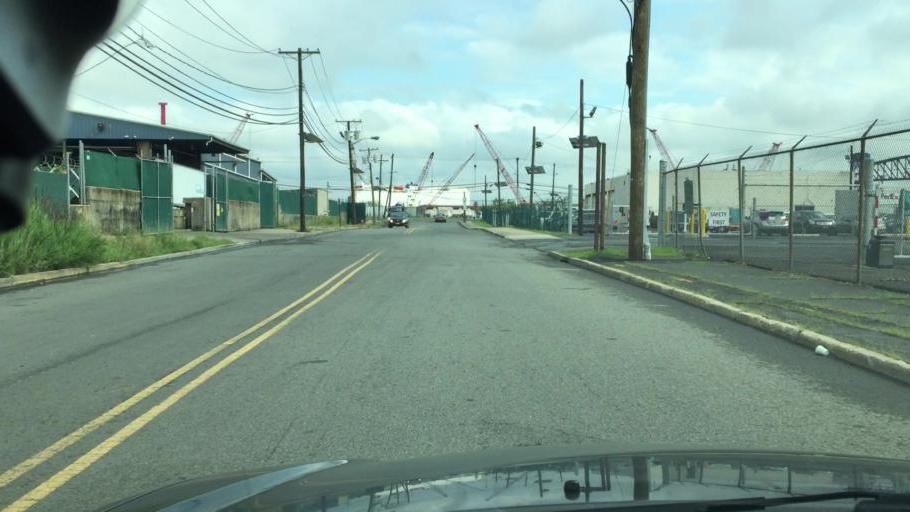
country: US
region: New Jersey
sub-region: Union County
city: Elizabeth
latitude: 40.6450
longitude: -74.1966
